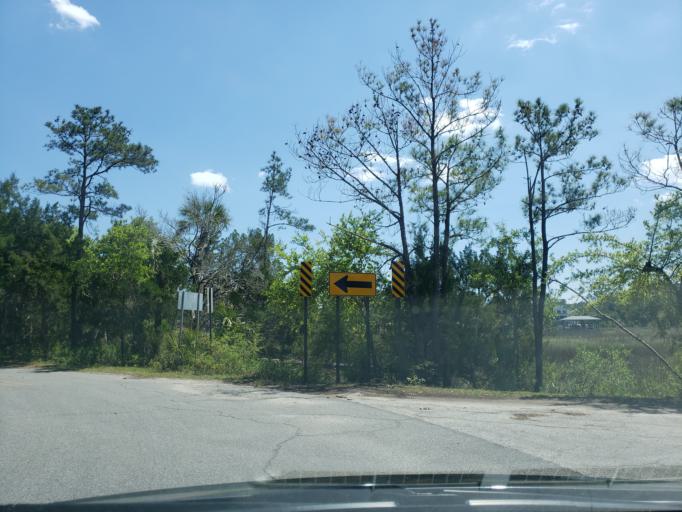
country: US
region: Georgia
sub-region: Chatham County
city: Whitemarsh Island
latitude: 32.0507
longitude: -81.0168
